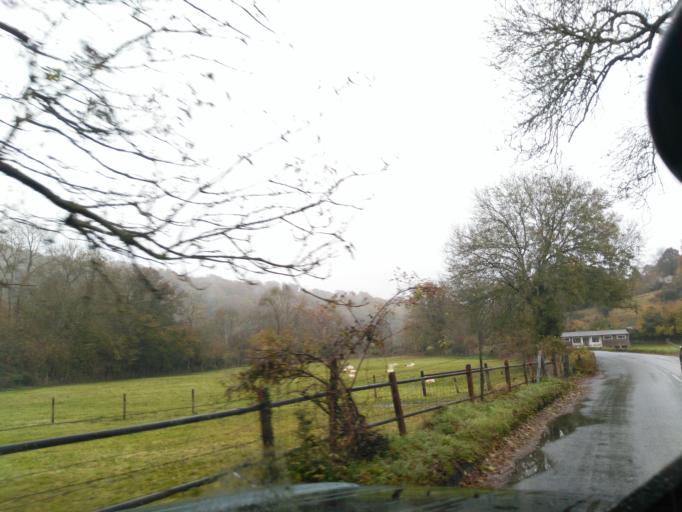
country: GB
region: England
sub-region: Bath and North East Somerset
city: Freshford
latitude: 51.3567
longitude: -2.3144
